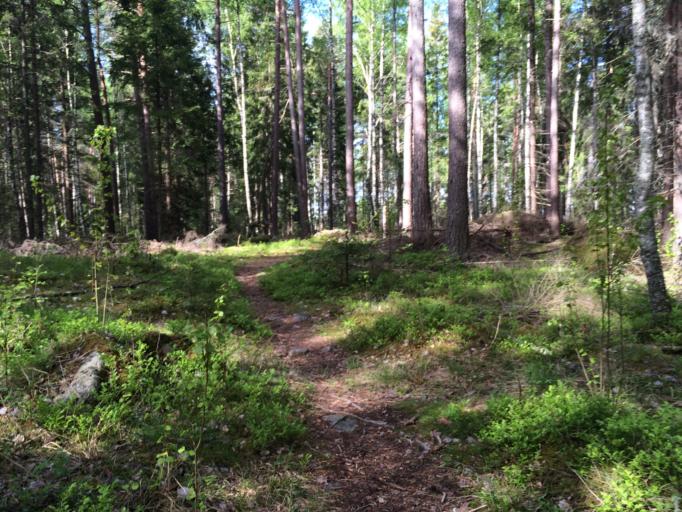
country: SE
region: Vaestmanland
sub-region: Hallstahammars Kommun
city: Hallstahammar
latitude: 59.6133
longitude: 16.2606
